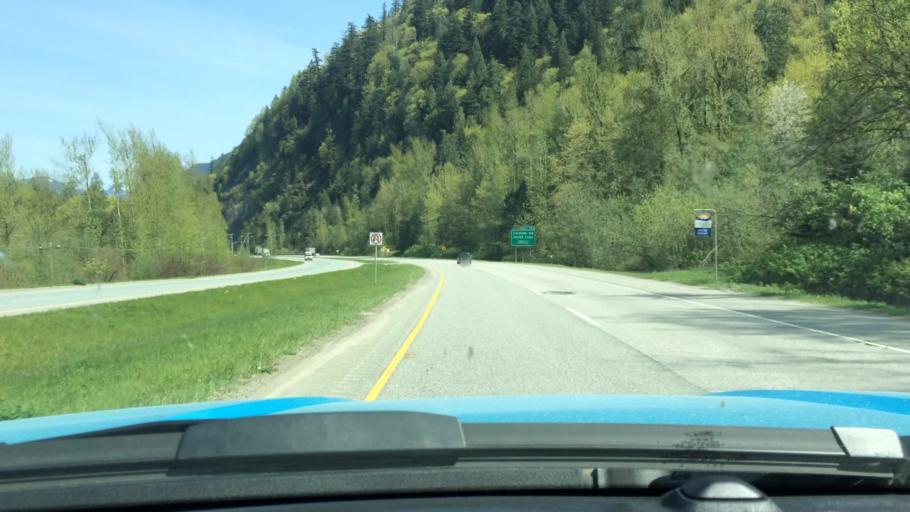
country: CA
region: British Columbia
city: Agassiz
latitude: 49.3002
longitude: -121.6494
